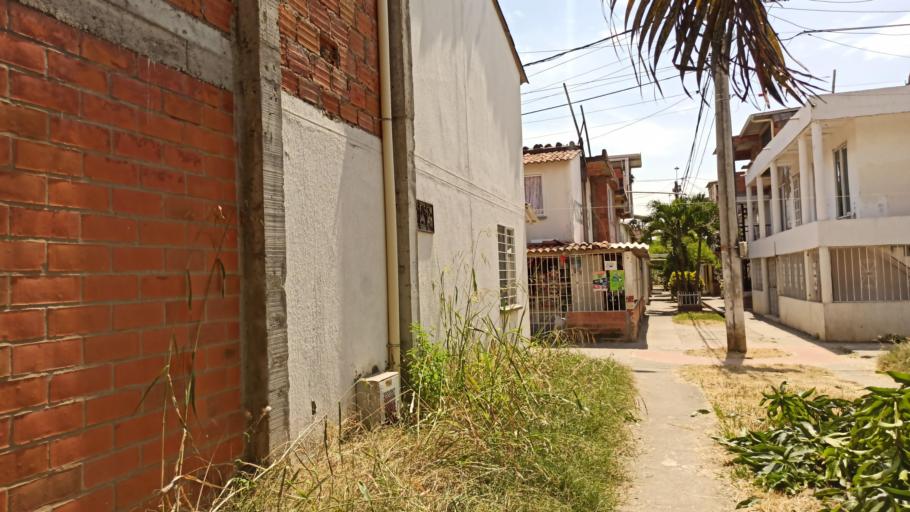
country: CO
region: Valle del Cauca
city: Jamundi
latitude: 3.2414
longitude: -76.5145
